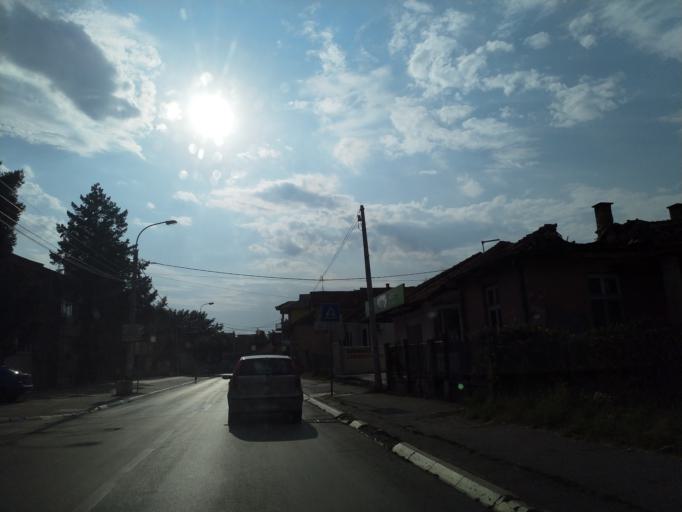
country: RS
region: Central Serbia
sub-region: Pomoravski Okrug
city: Paracin
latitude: 43.8648
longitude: 21.4144
